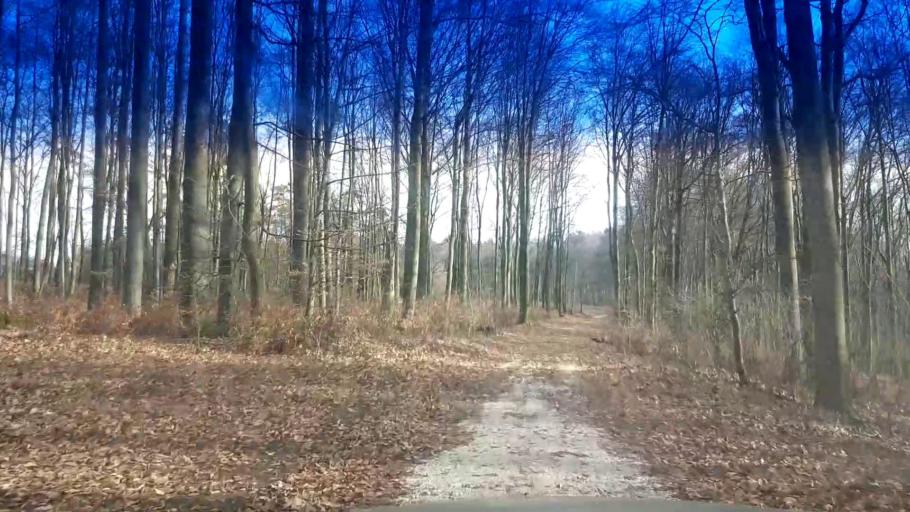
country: DE
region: Bavaria
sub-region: Upper Franconia
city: Litzendorf
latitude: 49.9272
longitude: 11.0644
